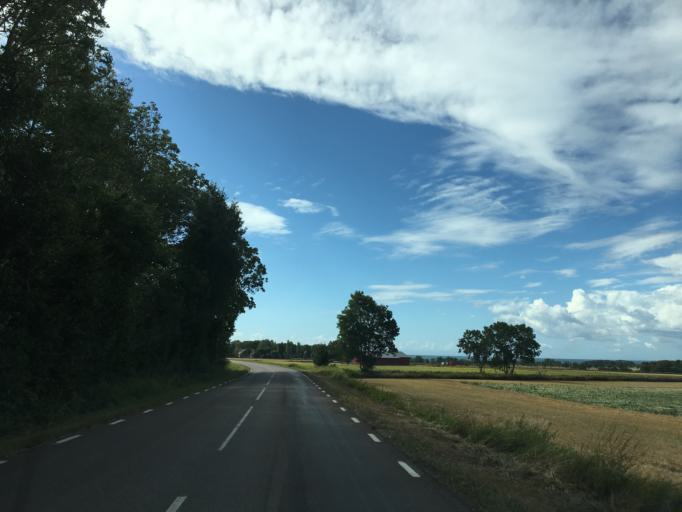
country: SE
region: Kalmar
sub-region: Morbylanga Kommun
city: Moerbylanga
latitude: 56.4372
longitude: 16.4204
